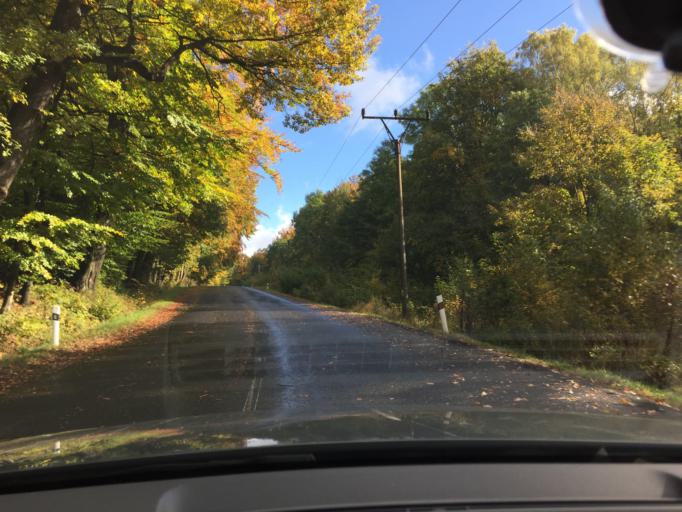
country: CZ
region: Ustecky
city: Chlumec
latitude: 50.7312
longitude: 13.9728
